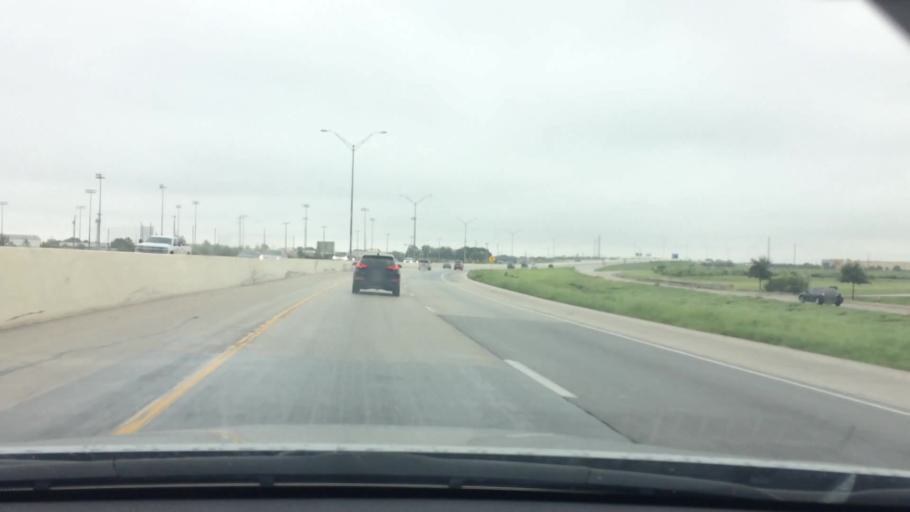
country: US
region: Texas
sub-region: Bexar County
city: Lackland Air Force Base
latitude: 29.4246
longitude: -98.5953
